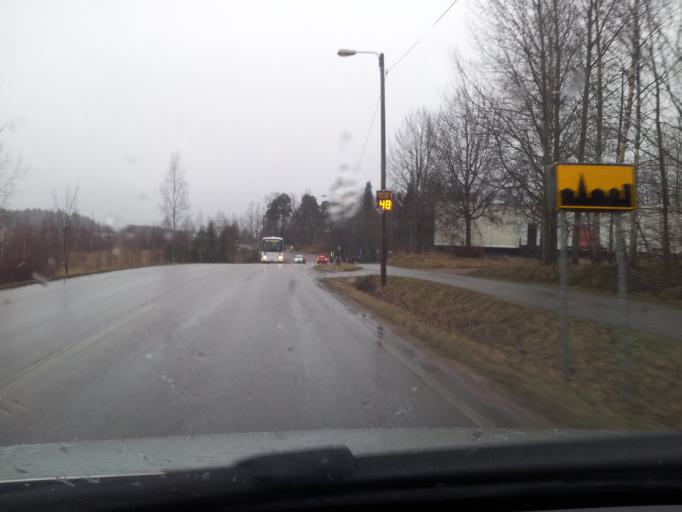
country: FI
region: Uusimaa
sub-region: Helsinki
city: Kirkkonummi
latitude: 60.1679
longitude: 24.5417
